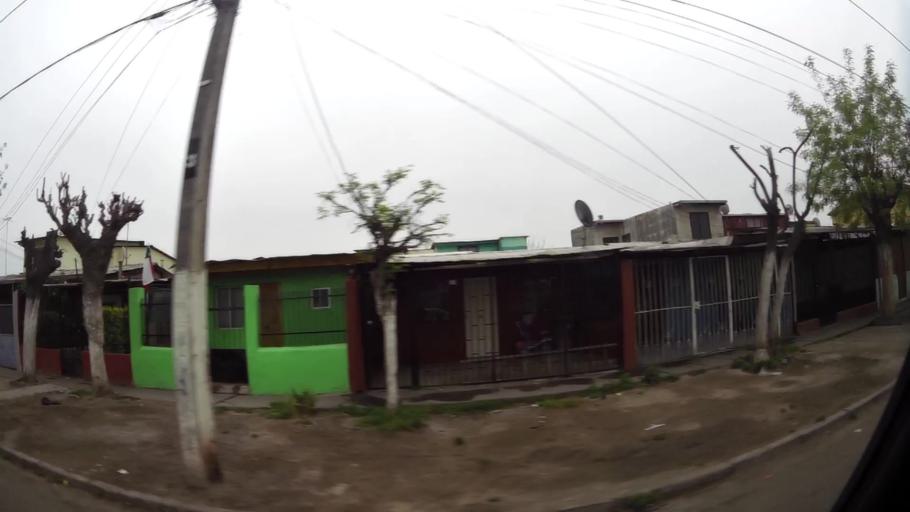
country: CL
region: Santiago Metropolitan
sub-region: Provincia de Santiago
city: Santiago
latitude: -33.4872
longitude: -70.6345
